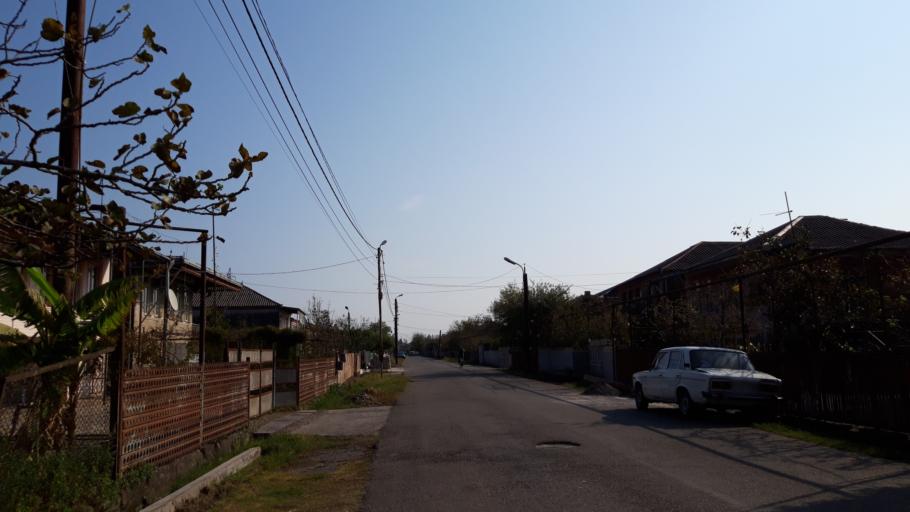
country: GE
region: Imereti
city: Samtredia
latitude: 42.1627
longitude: 42.3278
